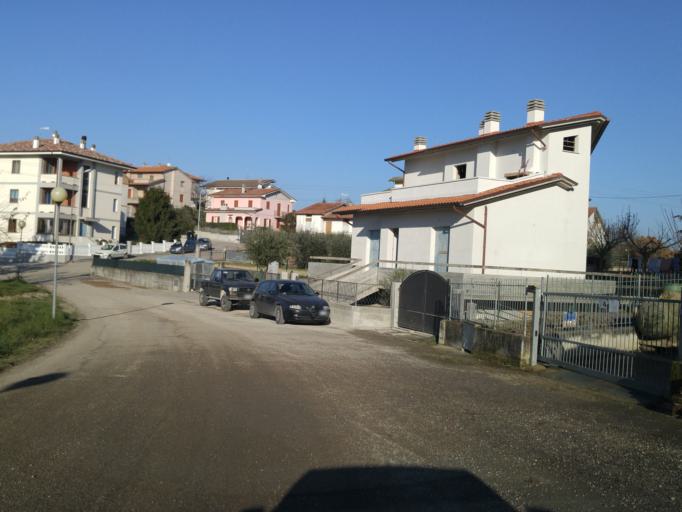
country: IT
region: The Marches
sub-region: Provincia di Pesaro e Urbino
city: Montefelcino
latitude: 43.7364
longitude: 12.8349
